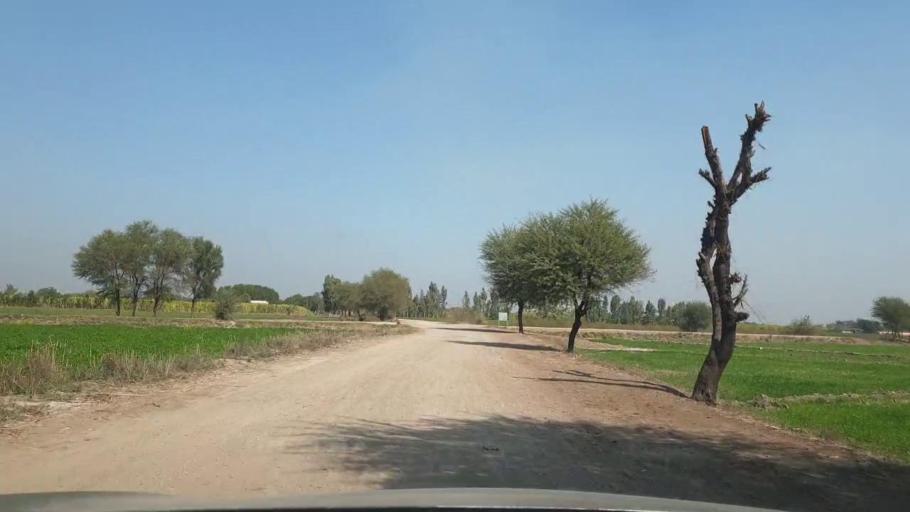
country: PK
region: Sindh
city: Tando Adam
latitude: 25.6076
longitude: 68.6426
